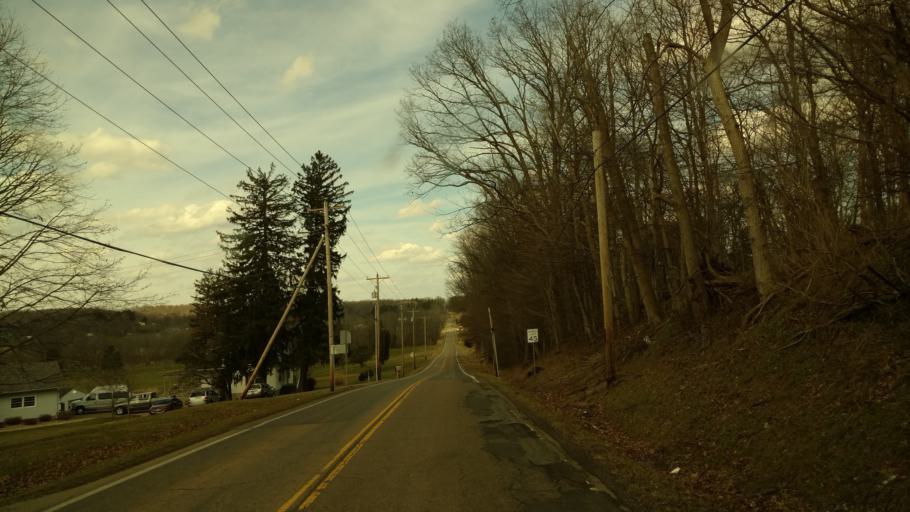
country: US
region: Ohio
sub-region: Knox County
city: Mount Vernon
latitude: 40.4065
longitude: -82.4565
